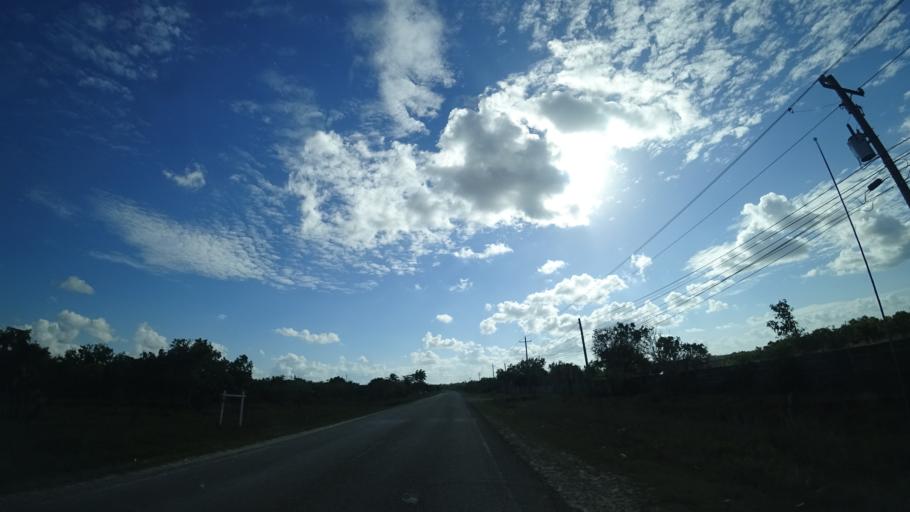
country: BZ
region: Belize
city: Belize City
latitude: 17.5580
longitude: -88.4058
